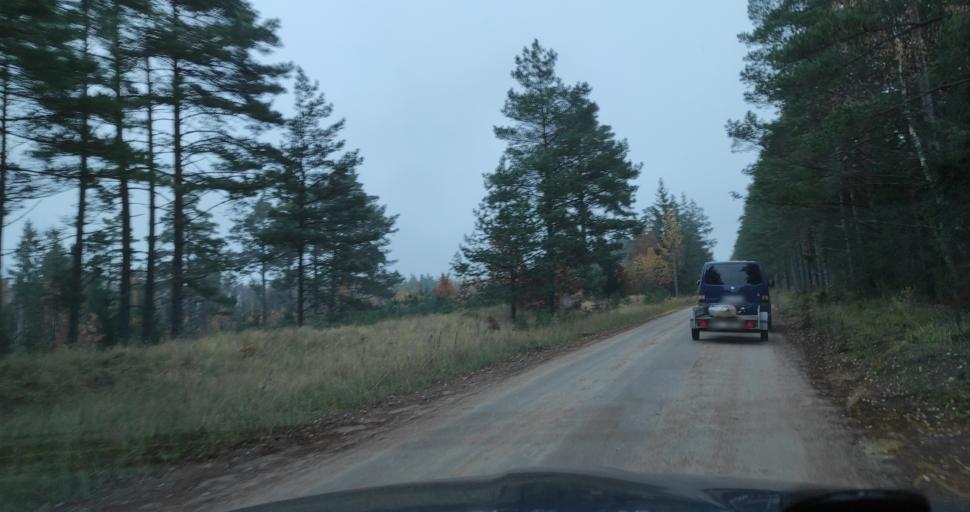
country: LV
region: Pavilostas
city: Pavilosta
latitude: 56.7541
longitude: 21.2627
